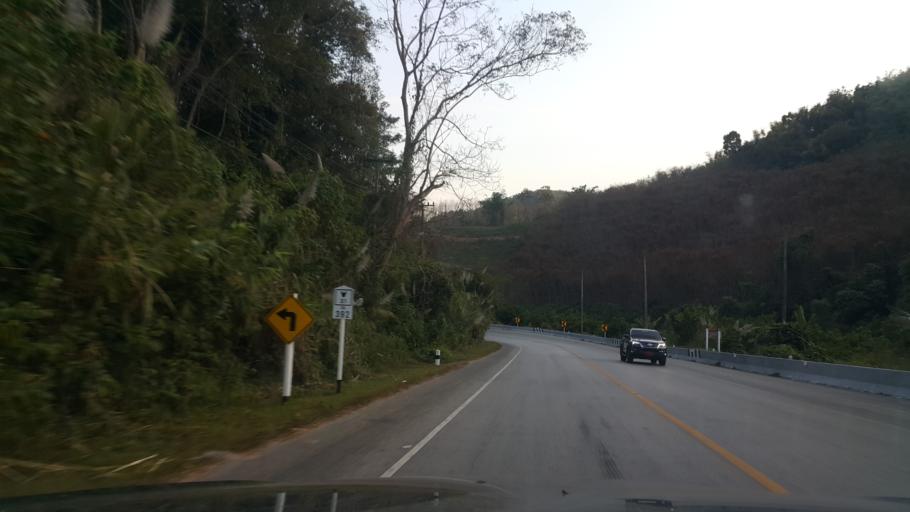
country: TH
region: Loei
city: Loei
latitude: 17.4766
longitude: 101.5612
